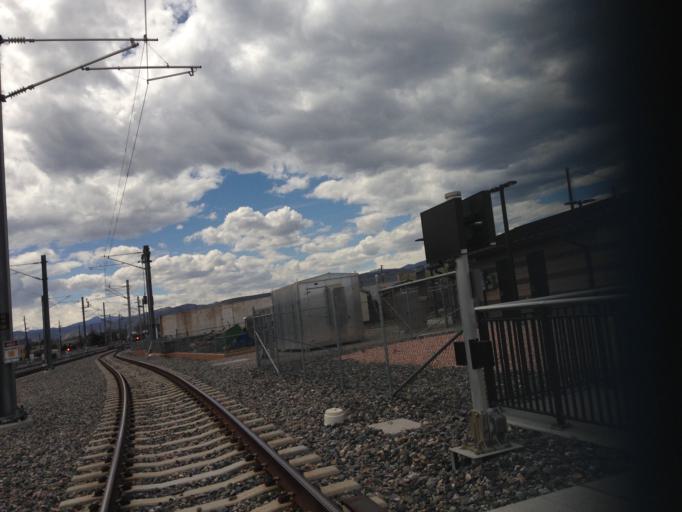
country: US
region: Colorado
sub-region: Jefferson County
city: Applewood
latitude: 39.7880
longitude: -105.1335
